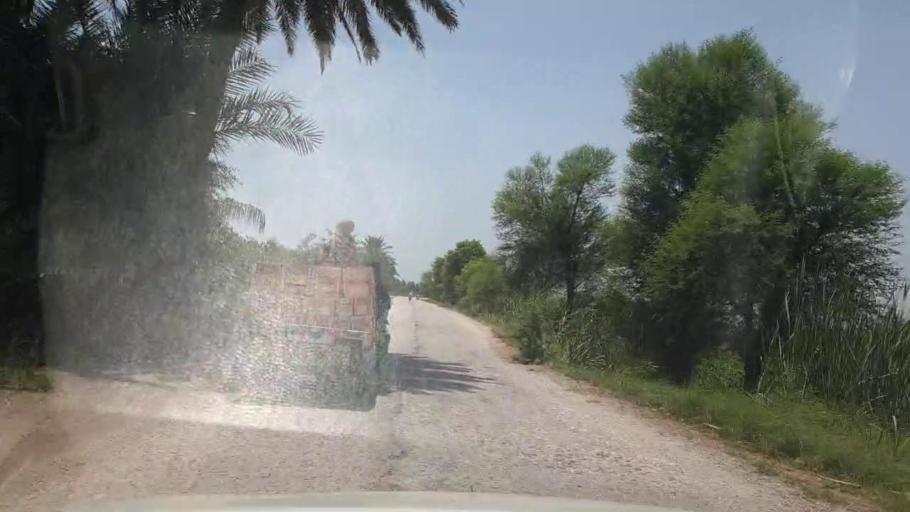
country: PK
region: Sindh
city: Bozdar
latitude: 27.1843
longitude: 68.6290
